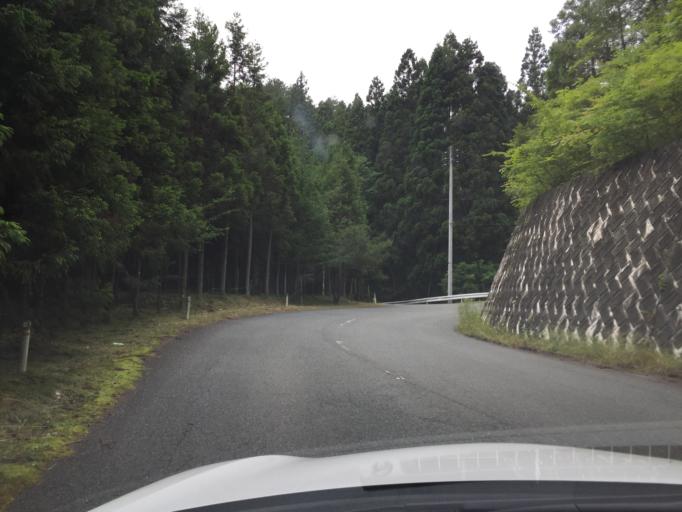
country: JP
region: Fukushima
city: Iwaki
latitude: 37.1481
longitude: 140.7005
